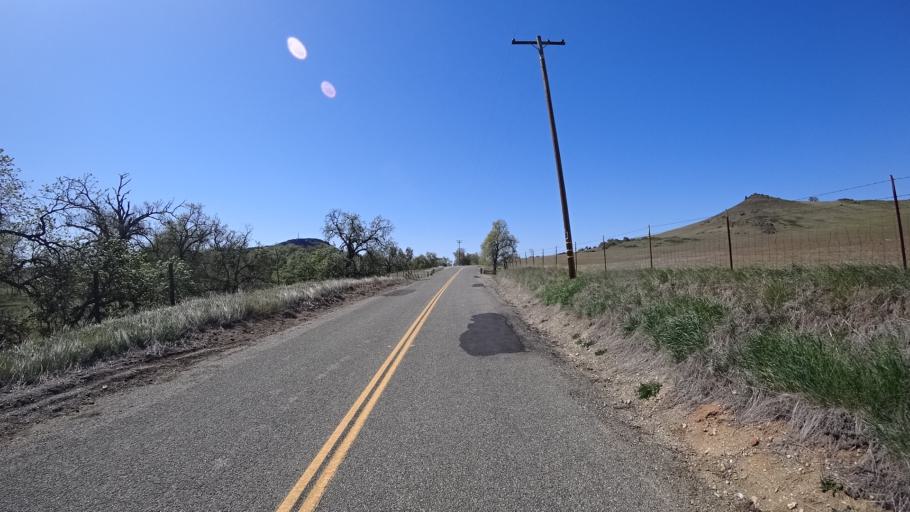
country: US
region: California
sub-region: Glenn County
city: Orland
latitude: 39.7681
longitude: -122.3266
